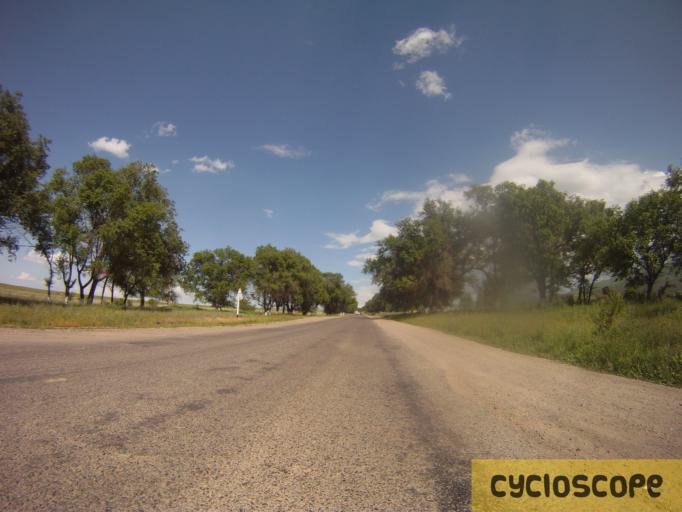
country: KZ
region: Almaty Oblysy
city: Turgen'
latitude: 43.3823
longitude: 77.5452
